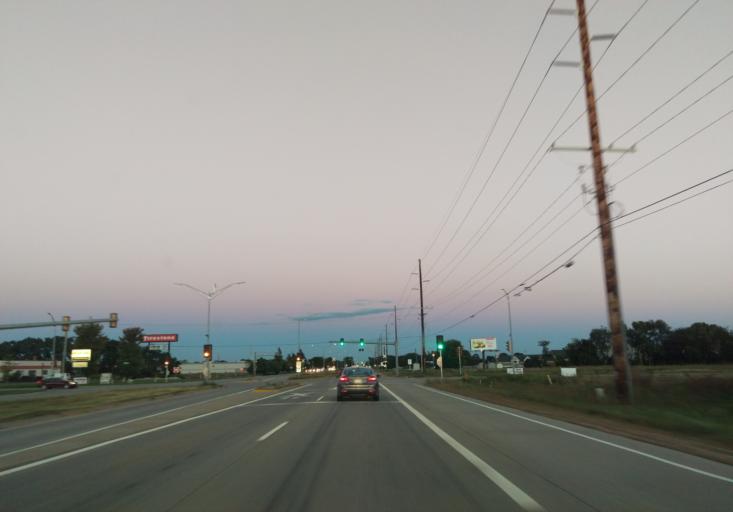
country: US
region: Wisconsin
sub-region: Rock County
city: Janesville
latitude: 42.7250
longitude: -89.0143
